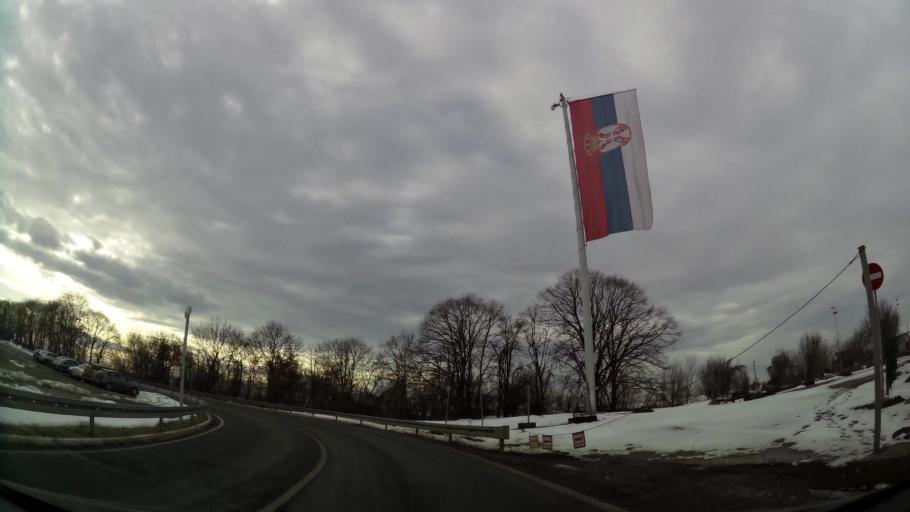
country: RS
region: Central Serbia
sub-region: Belgrade
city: Surcin
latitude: 44.8157
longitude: 20.2874
